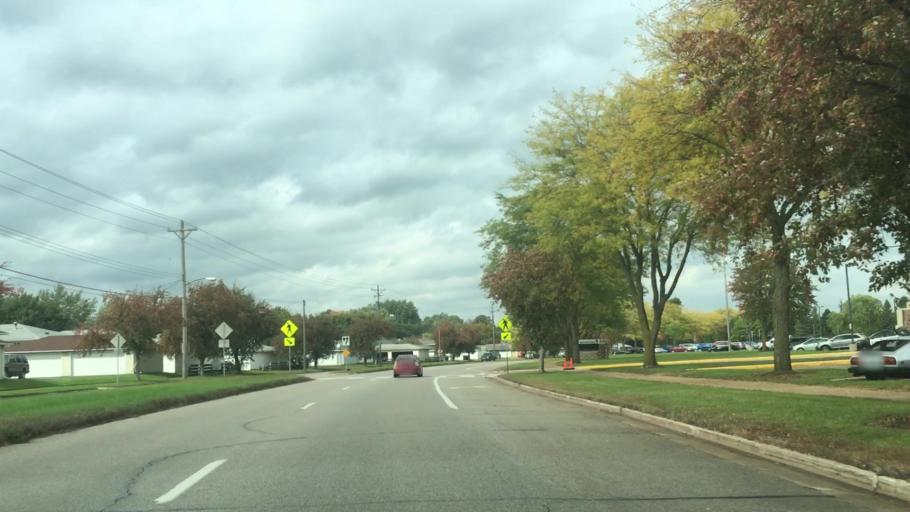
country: US
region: Minnesota
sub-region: Olmsted County
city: Rochester
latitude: 44.0021
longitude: -92.4476
